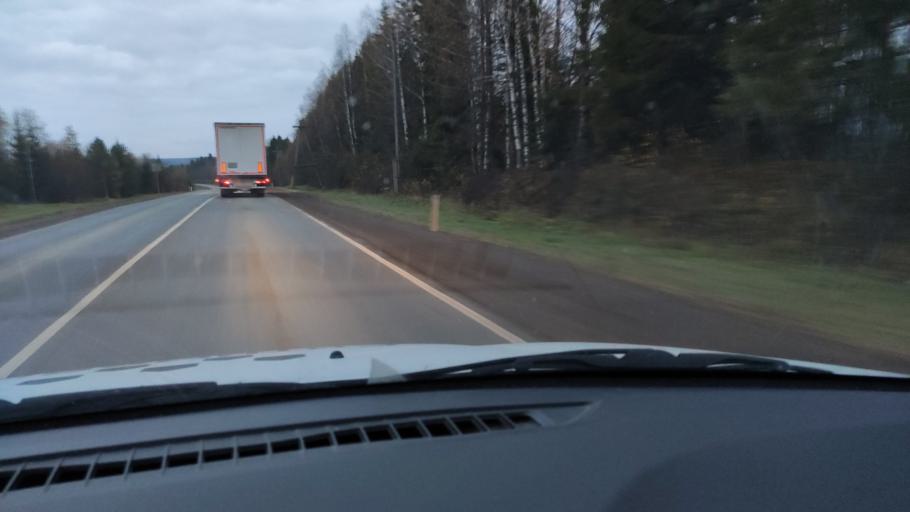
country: RU
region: Kirov
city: Kostino
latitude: 58.8568
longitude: 53.1893
